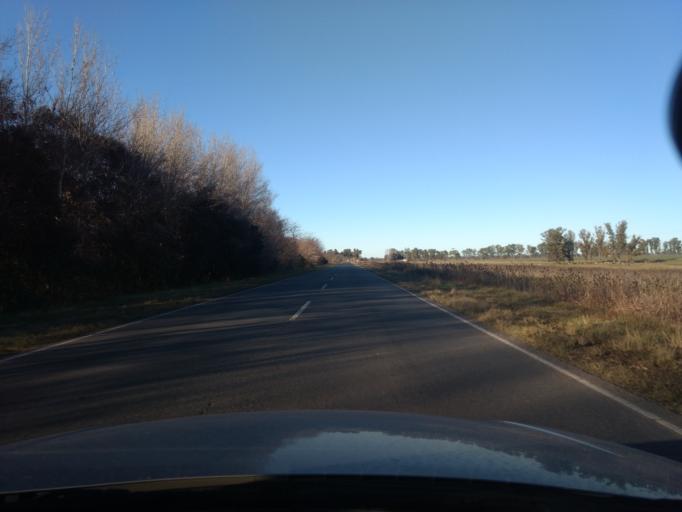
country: AR
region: Buenos Aires
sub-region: Partido de Lujan
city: Lujan
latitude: -34.6159
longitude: -59.1066
